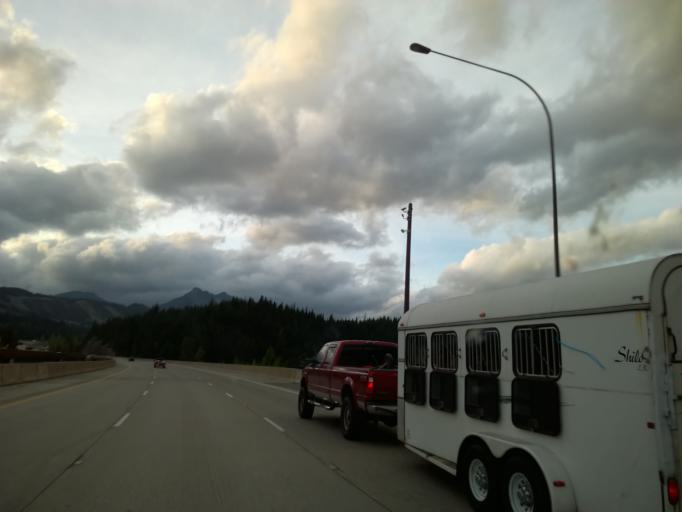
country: US
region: Washington
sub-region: King County
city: Tanner
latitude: 47.3901
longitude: -121.3824
